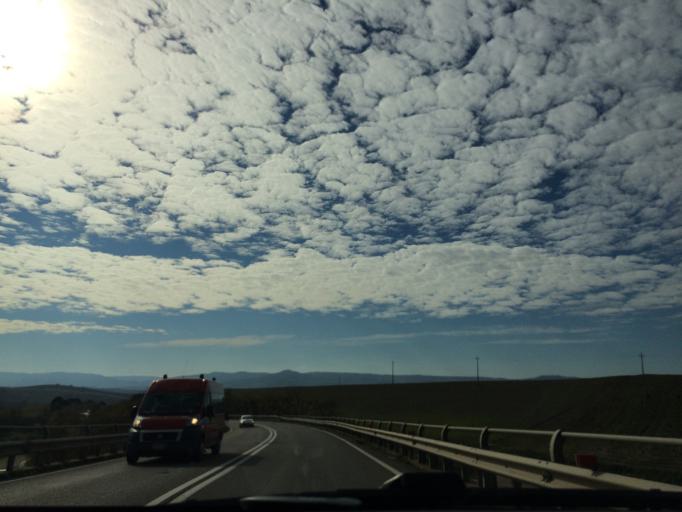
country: IT
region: Basilicate
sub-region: Provincia di Matera
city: Matera
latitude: 40.6336
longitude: 16.5928
